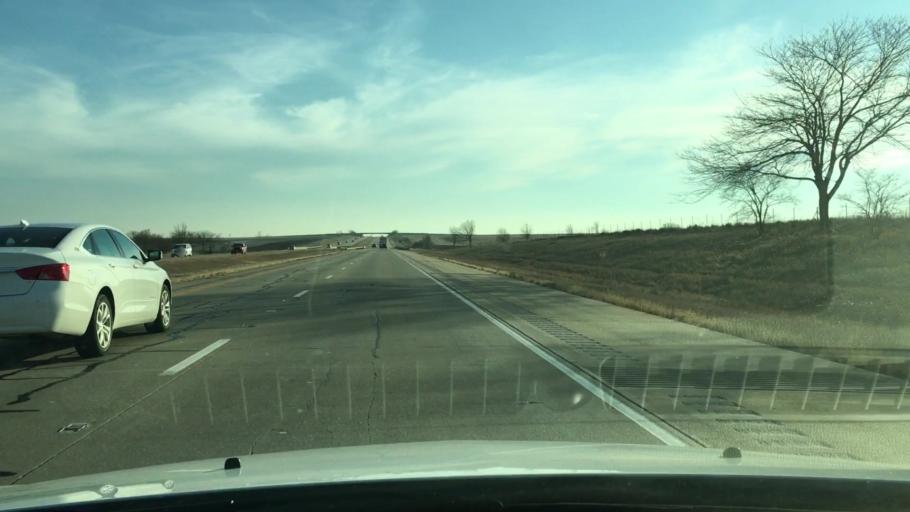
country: US
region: Illinois
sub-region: Woodford County
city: El Paso
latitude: 40.8032
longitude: -89.0359
